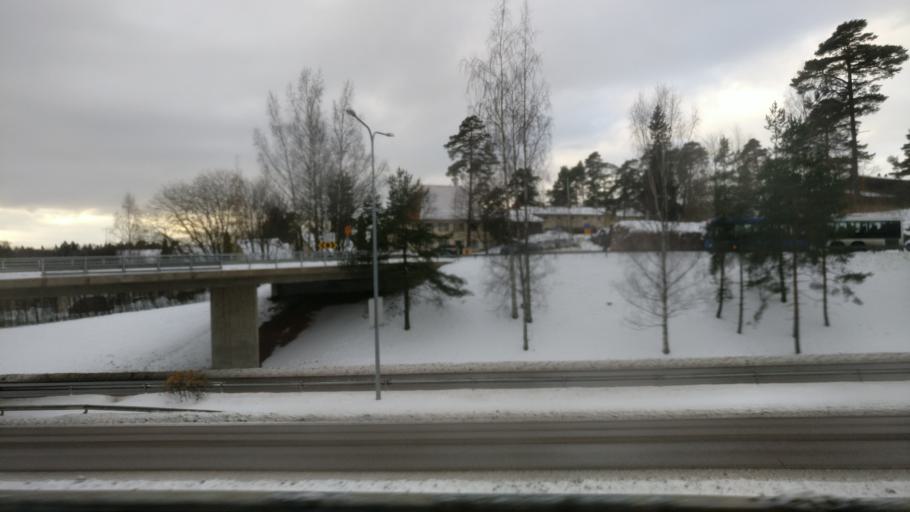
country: FI
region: Uusimaa
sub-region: Helsinki
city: Vantaa
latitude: 60.1845
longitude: 25.0478
